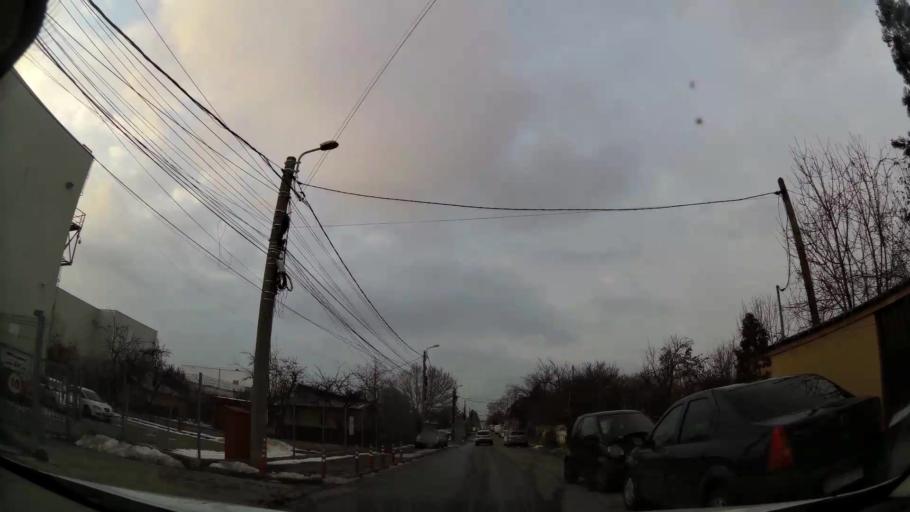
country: RO
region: Ilfov
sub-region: Comuna Fundeni-Dobroesti
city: Fundeni
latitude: 44.4692
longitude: 26.1654
